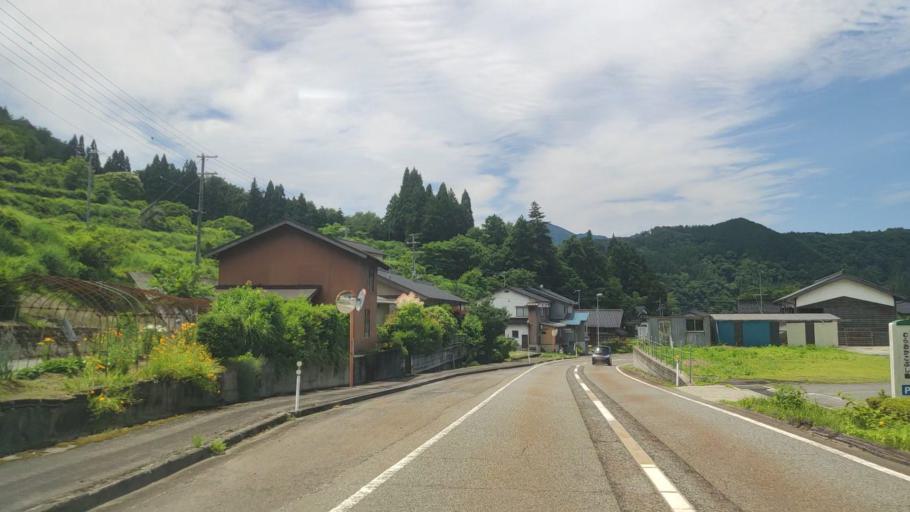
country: JP
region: Hyogo
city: Toyooka
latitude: 35.4756
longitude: 134.6002
